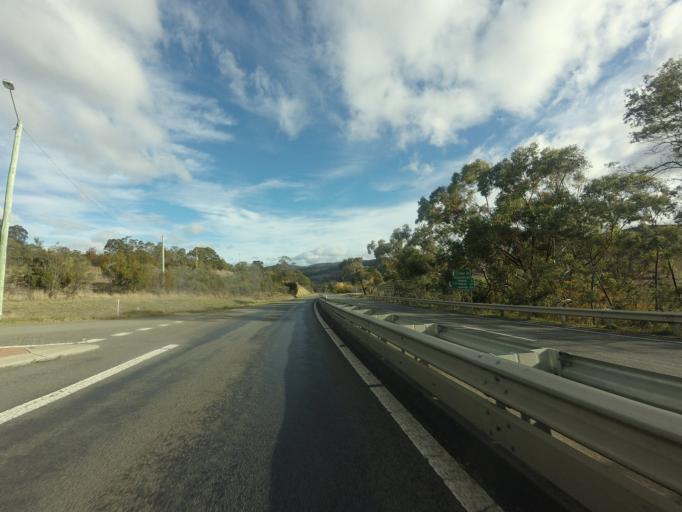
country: AU
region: Tasmania
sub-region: Brighton
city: Bridgewater
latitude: -42.5830
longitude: 147.2284
